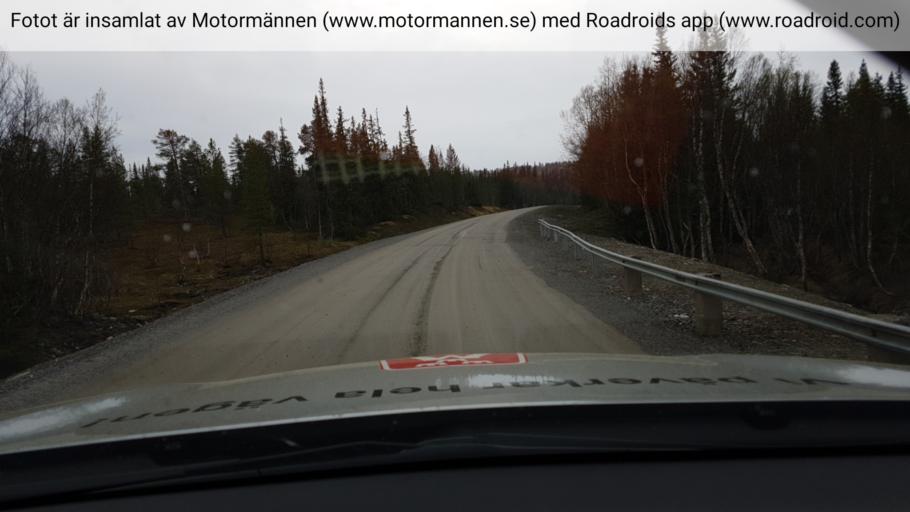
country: NO
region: Nord-Trondelag
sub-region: Snasa
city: Snaase
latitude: 63.7028
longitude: 12.3492
